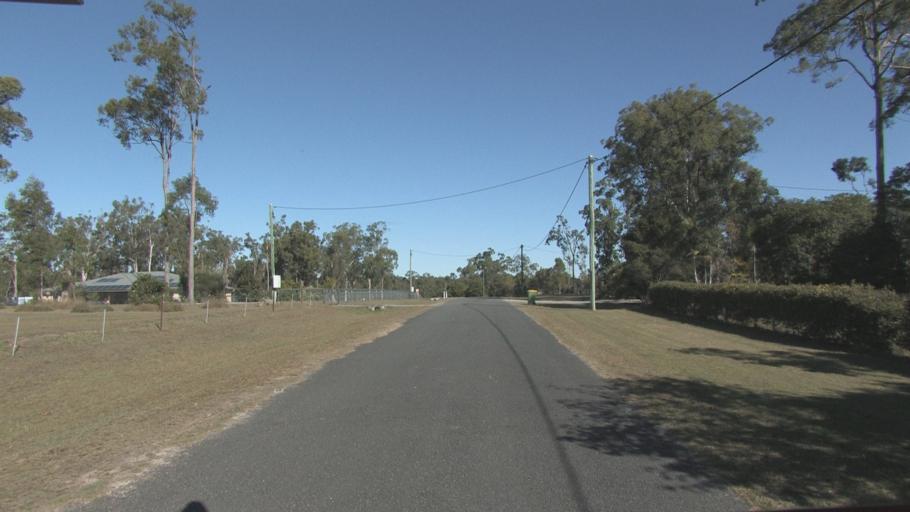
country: AU
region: Queensland
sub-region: Logan
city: Chambers Flat
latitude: -27.7275
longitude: 153.0670
